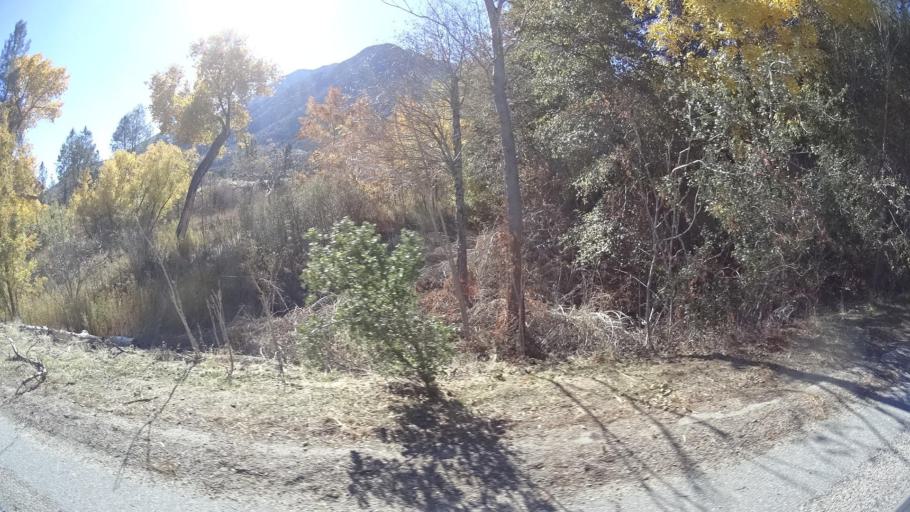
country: US
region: California
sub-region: Kern County
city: Kernville
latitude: 35.7812
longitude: -118.4402
